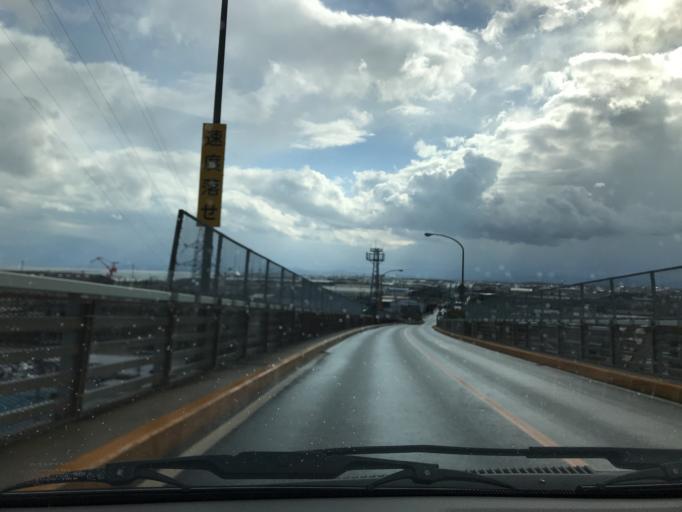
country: JP
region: Shimane
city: Sakaiminato
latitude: 35.5462
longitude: 133.2457
